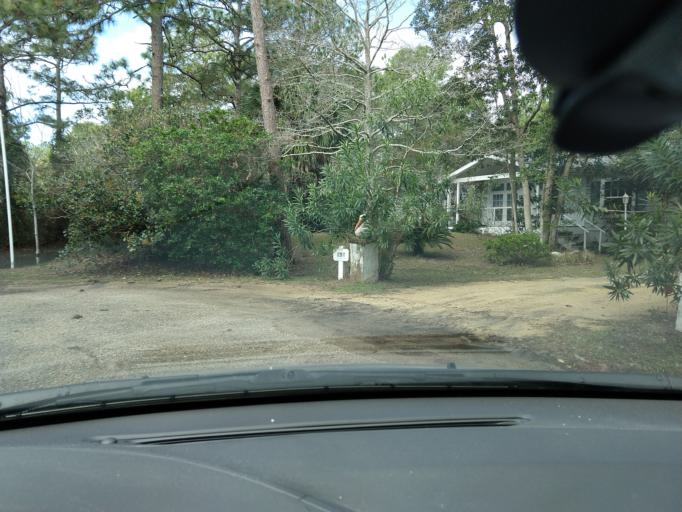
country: US
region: Florida
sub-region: Walton County
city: Miramar Beach
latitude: 30.3927
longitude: -86.3083
